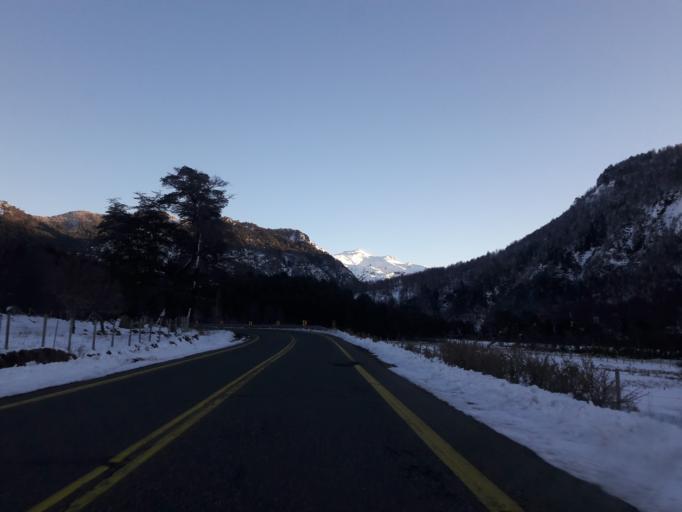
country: CL
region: Araucania
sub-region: Provincia de Cautin
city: Vilcun
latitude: -38.5010
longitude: -71.5198
